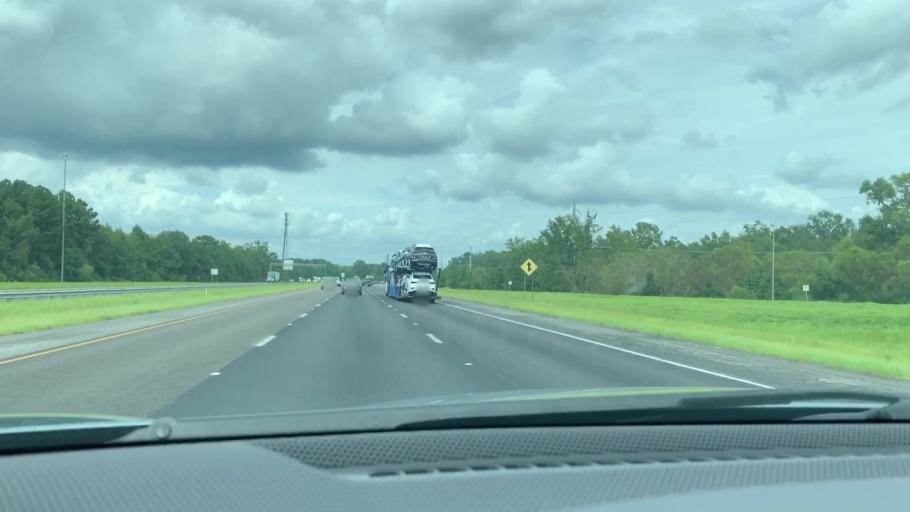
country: US
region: Georgia
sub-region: Liberty County
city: Midway
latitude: 31.7801
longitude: -81.3783
